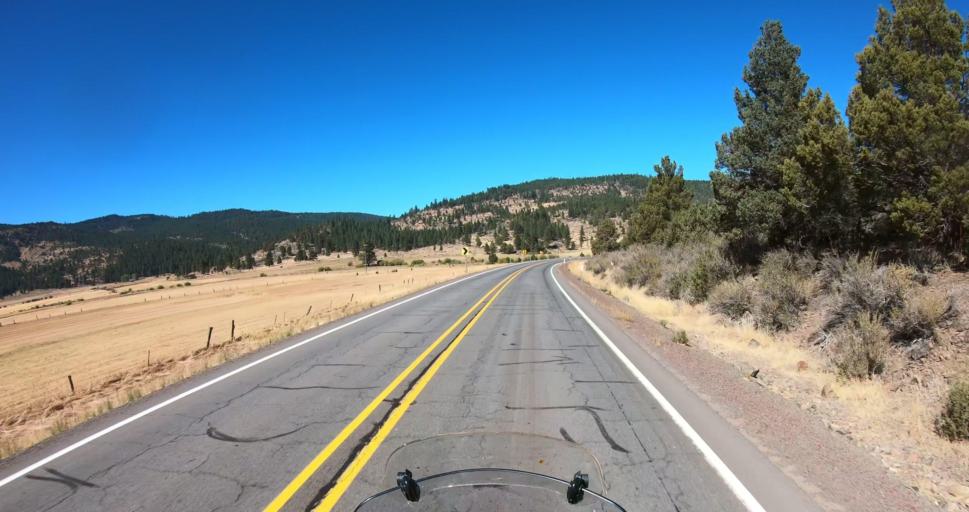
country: US
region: Oregon
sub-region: Lake County
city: Lakeview
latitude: 42.3825
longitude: -120.3052
